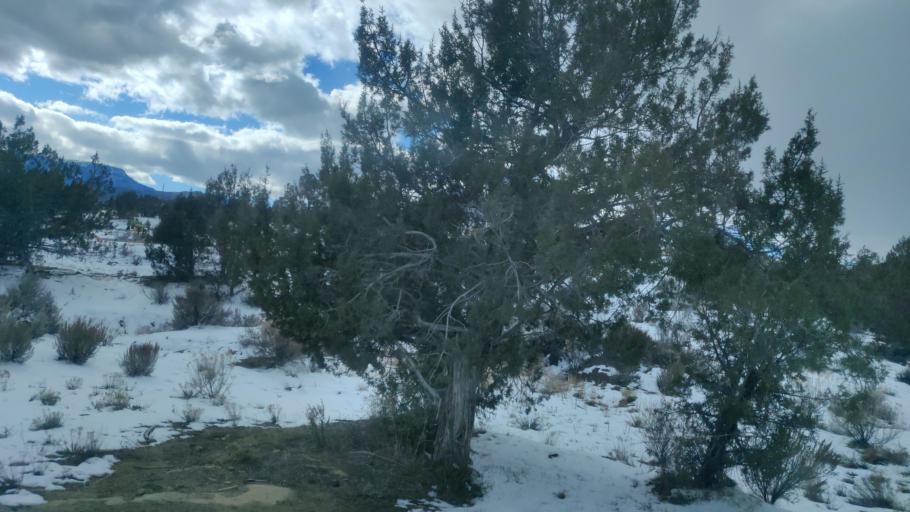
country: US
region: Colorado
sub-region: Mesa County
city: Palisade
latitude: 39.2071
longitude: -108.1466
